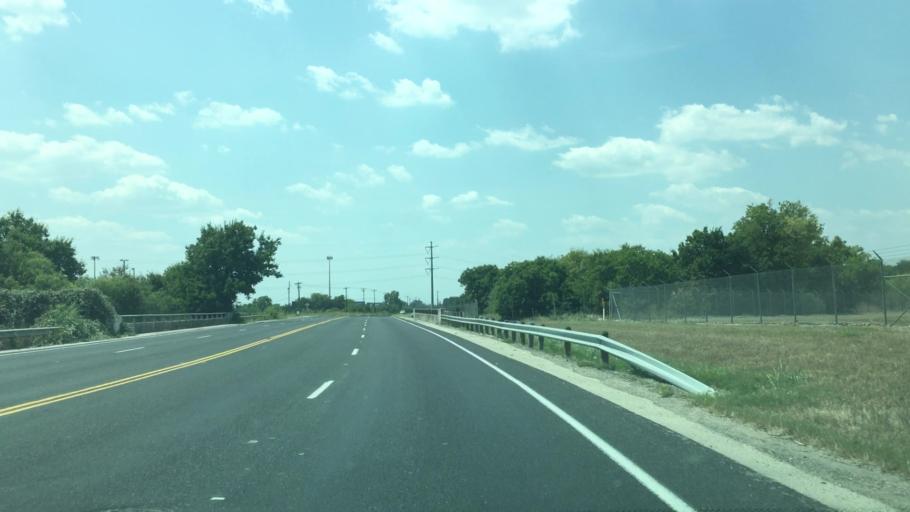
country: US
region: Texas
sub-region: Travis County
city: Austin
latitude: 30.1779
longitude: -97.6817
